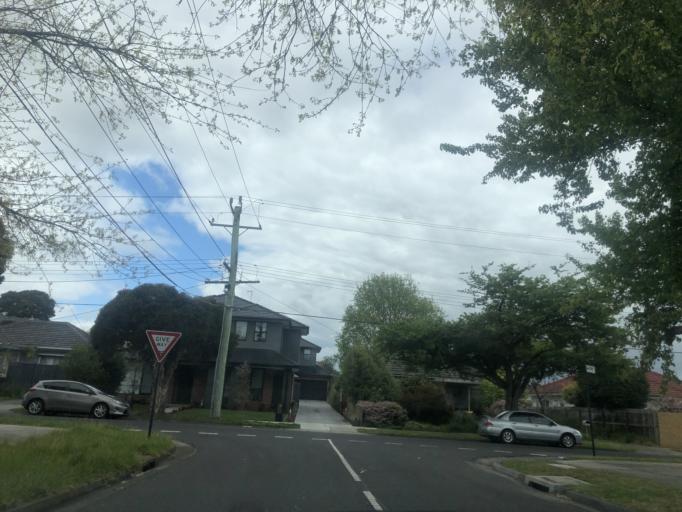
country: AU
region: Victoria
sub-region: Kingston
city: Clayton South
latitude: -37.9261
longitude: 145.1091
